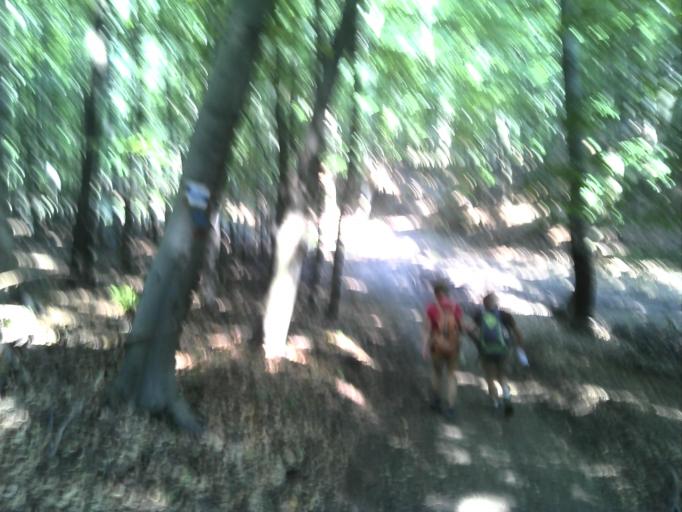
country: HU
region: Komarom-Esztergom
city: Oroszlany
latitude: 47.4434
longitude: 18.3648
